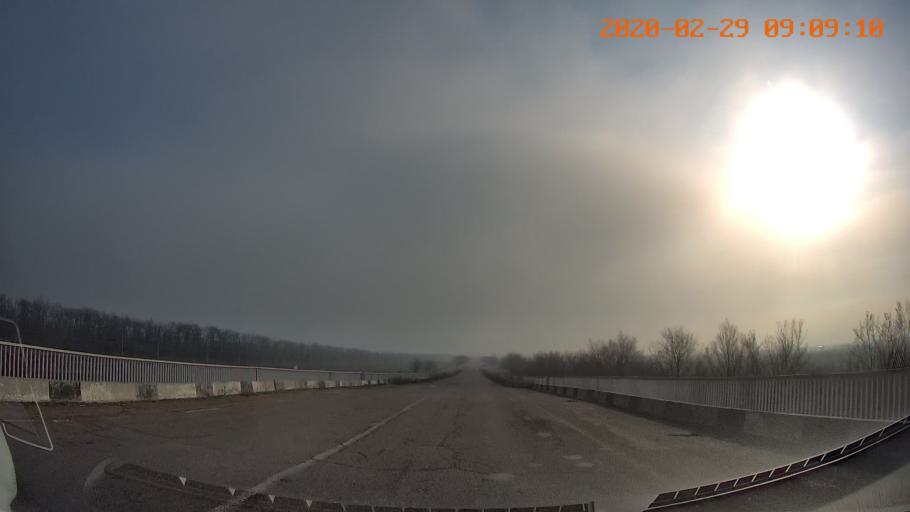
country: MD
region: Telenesti
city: Slobozia
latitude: 46.8452
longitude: 29.7584
